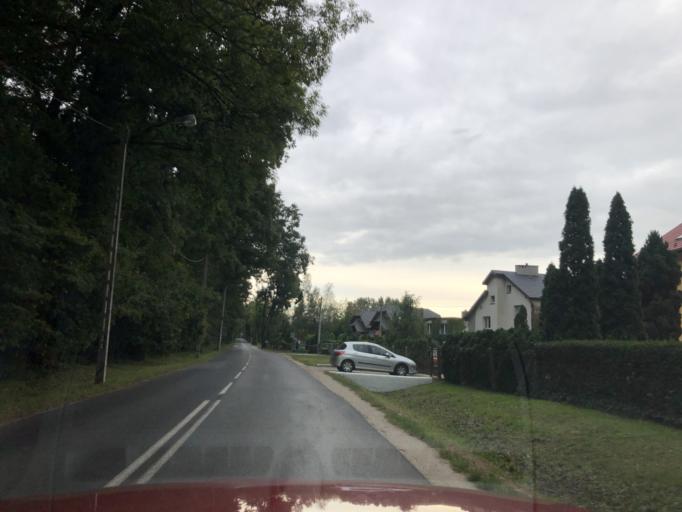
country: PL
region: Lower Silesian Voivodeship
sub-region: Powiat wroclawski
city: Dlugoleka
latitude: 51.1914
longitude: 17.1839
